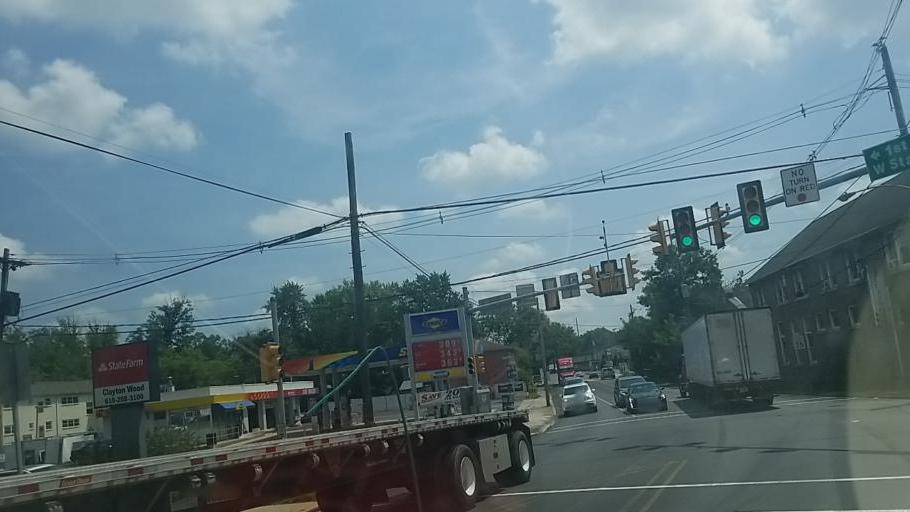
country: US
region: Pennsylvania
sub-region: Chester County
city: Avondale
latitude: 39.8249
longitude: -75.7834
